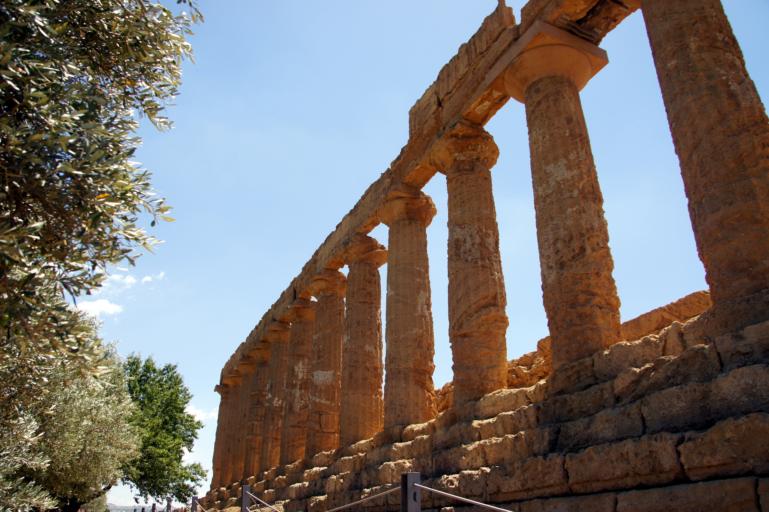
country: IT
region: Sicily
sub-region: Agrigento
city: San Leone Mose
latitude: 37.2887
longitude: 13.6000
